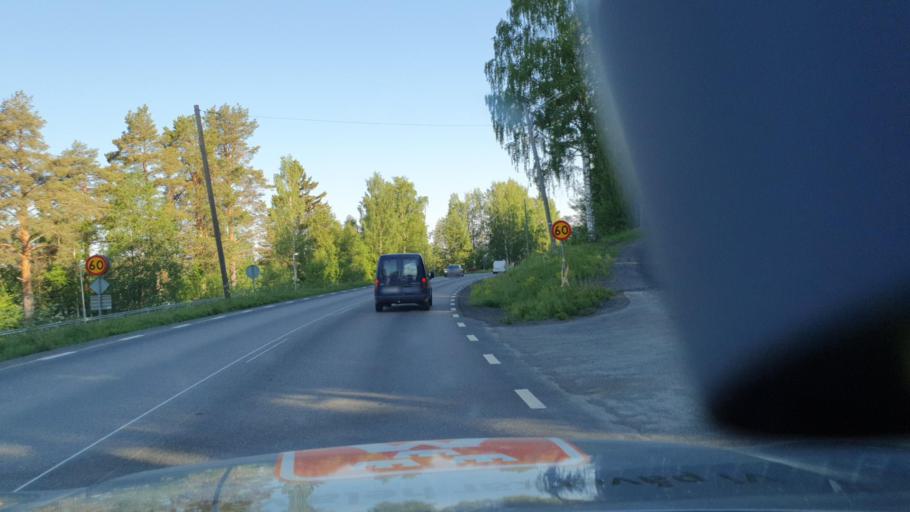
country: SE
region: Norrbotten
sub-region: Bodens Kommun
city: Boden
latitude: 65.8334
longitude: 21.6150
